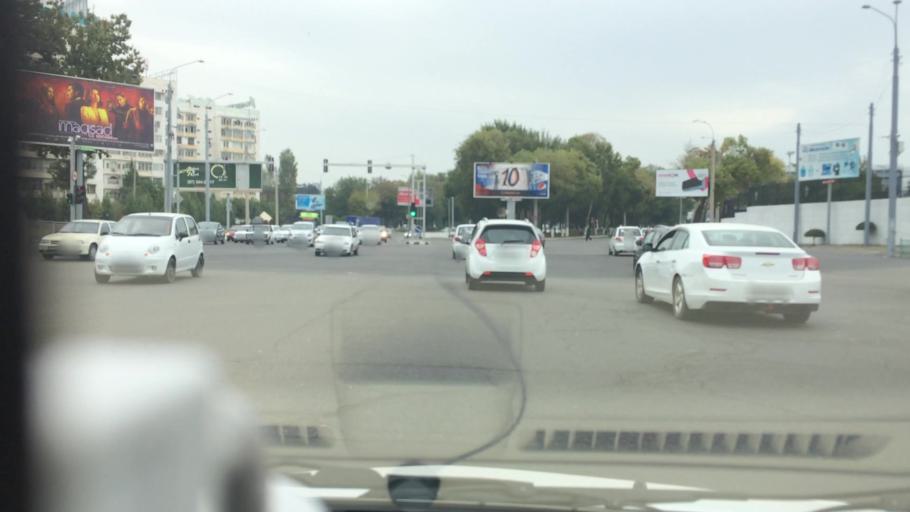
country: UZ
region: Toshkent Shahri
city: Tashkent
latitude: 41.2888
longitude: 69.2820
